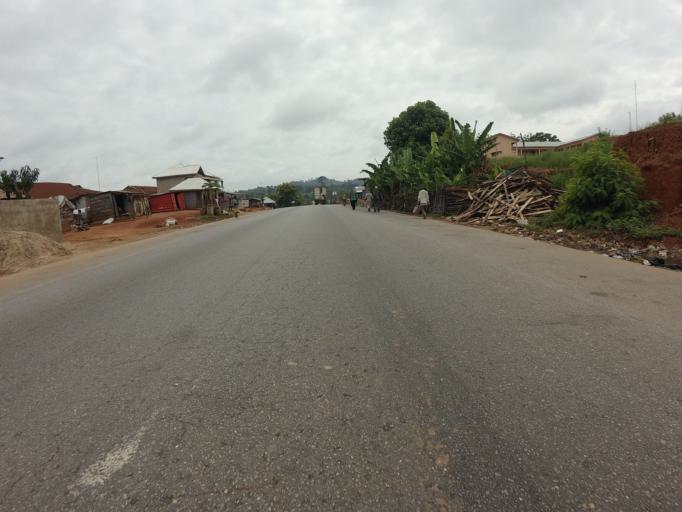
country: GH
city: Bechem
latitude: 7.1366
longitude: -1.7351
